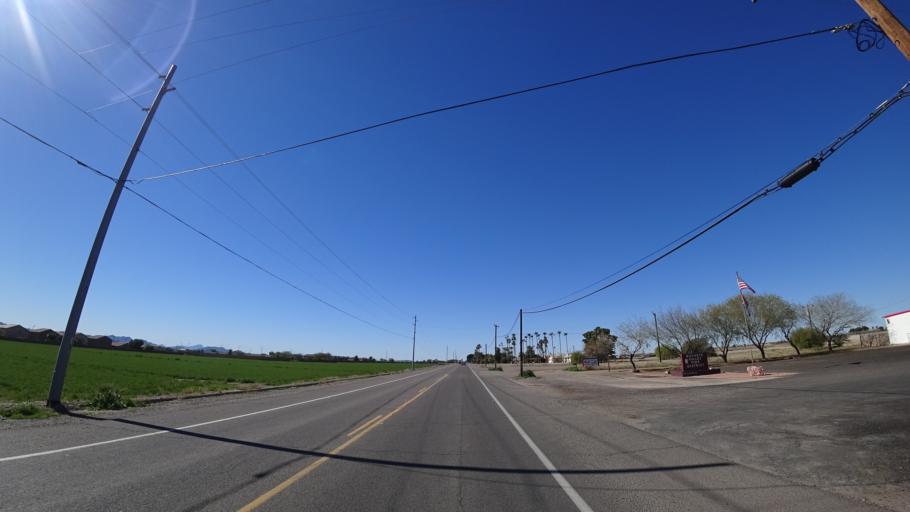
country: US
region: Arizona
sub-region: Maricopa County
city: Buckeye
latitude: 33.3704
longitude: -112.5926
